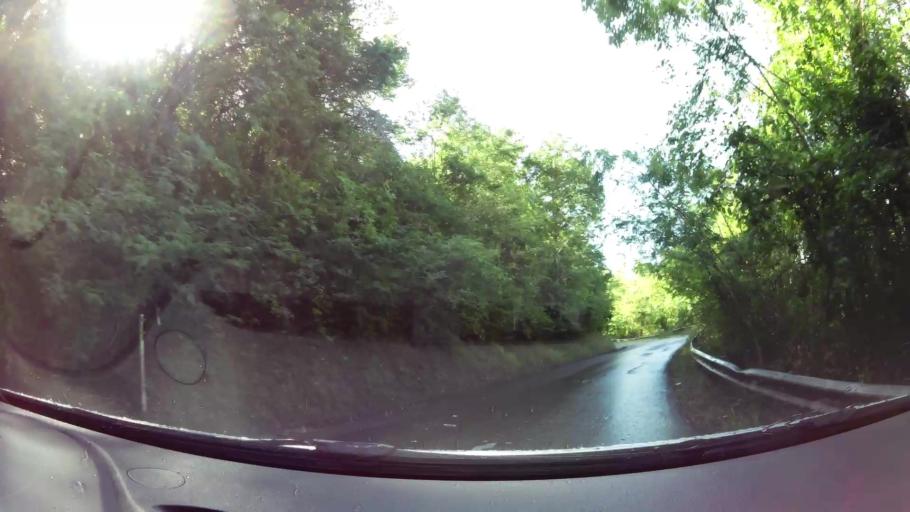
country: MQ
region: Martinique
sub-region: Martinique
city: Les Trois-Ilets
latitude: 14.4785
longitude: -61.0762
